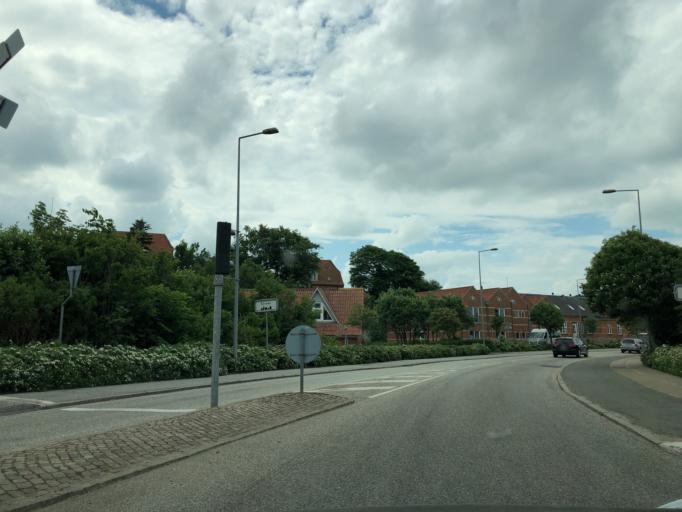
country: DK
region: Central Jutland
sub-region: Struer Kommune
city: Struer
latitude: 56.4939
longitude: 8.5859
